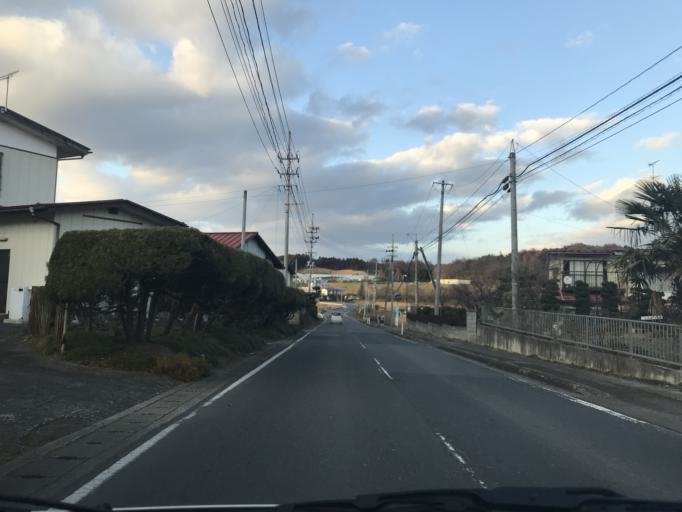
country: JP
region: Miyagi
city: Furukawa
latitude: 38.6631
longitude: 141.0114
